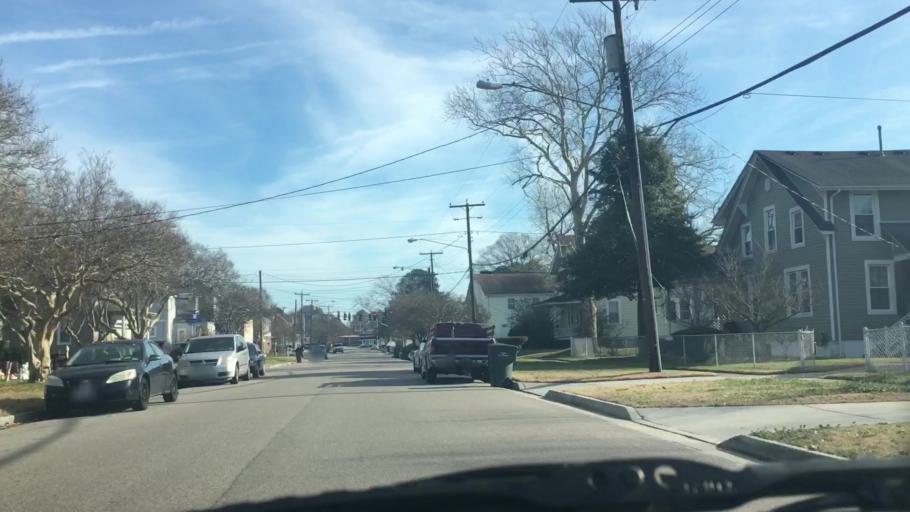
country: US
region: Virginia
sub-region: City of Norfolk
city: Norfolk
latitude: 36.8675
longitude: -76.2530
